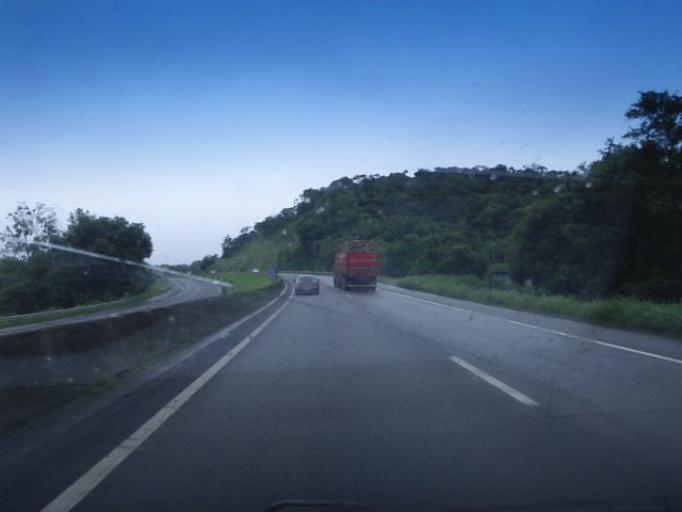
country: BR
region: Sao Paulo
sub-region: Cajati
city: Cajati
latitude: -24.7502
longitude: -48.1523
